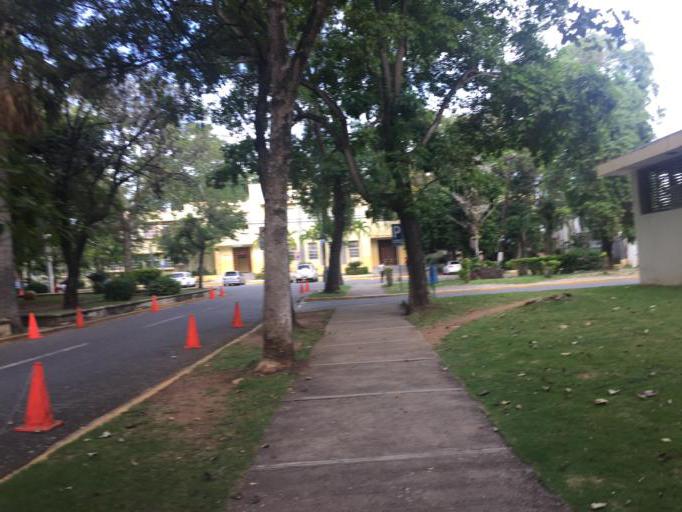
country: DO
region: Nacional
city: Ciudad Nueva
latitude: 18.4607
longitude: -69.9152
